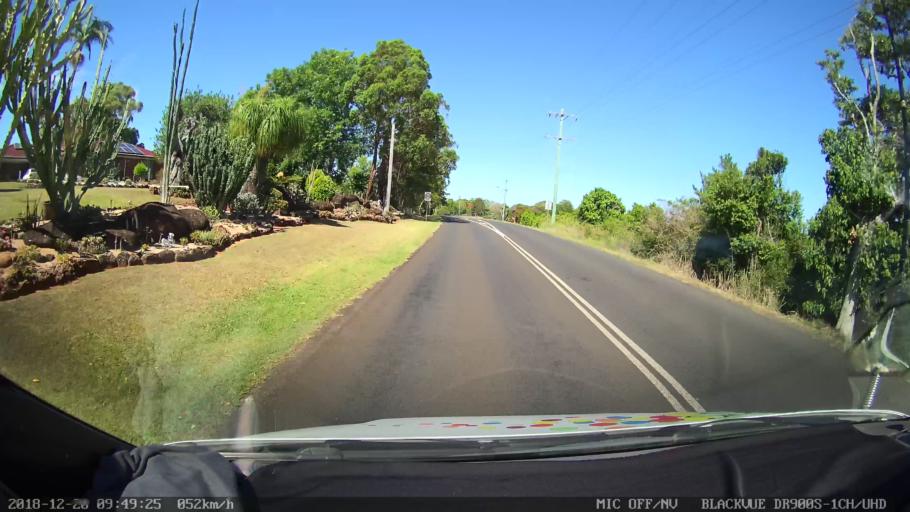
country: AU
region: New South Wales
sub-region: Lismore Municipality
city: Lismore
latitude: -28.7741
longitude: 153.2858
